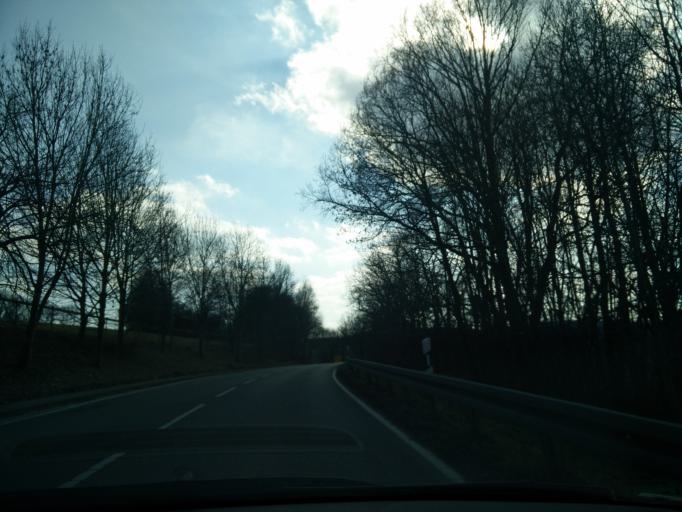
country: DE
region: Saxony
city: Seelitz
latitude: 51.0467
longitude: 12.8117
